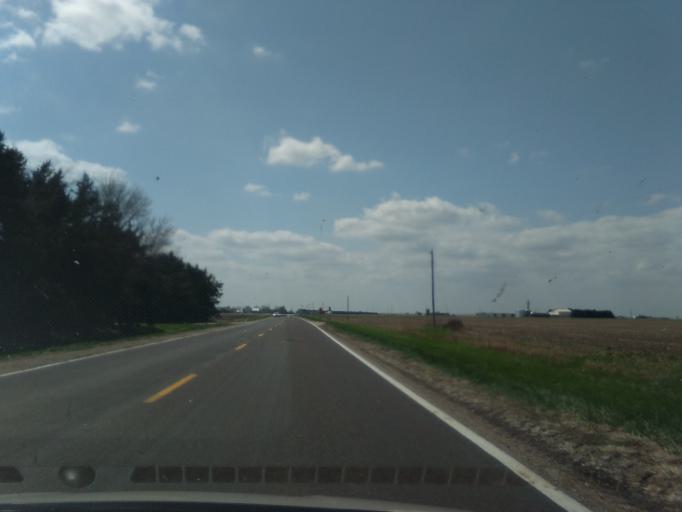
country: US
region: Nebraska
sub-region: Thayer County
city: Hebron
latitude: 40.3217
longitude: -97.5693
